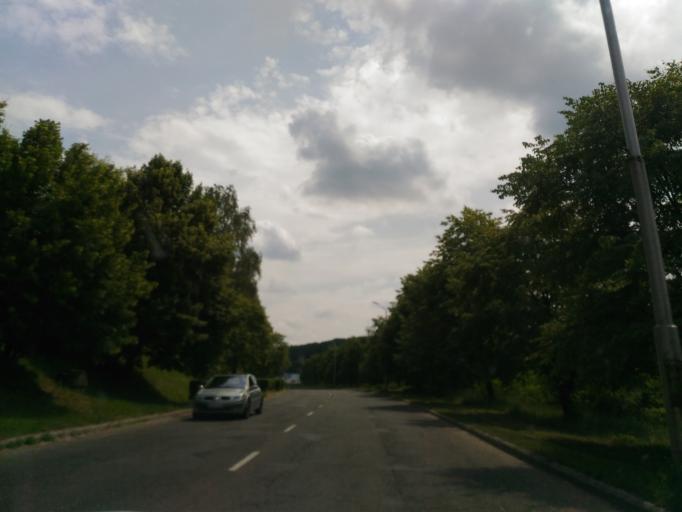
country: HU
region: Baranya
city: Komlo
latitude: 46.1958
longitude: 18.2527
